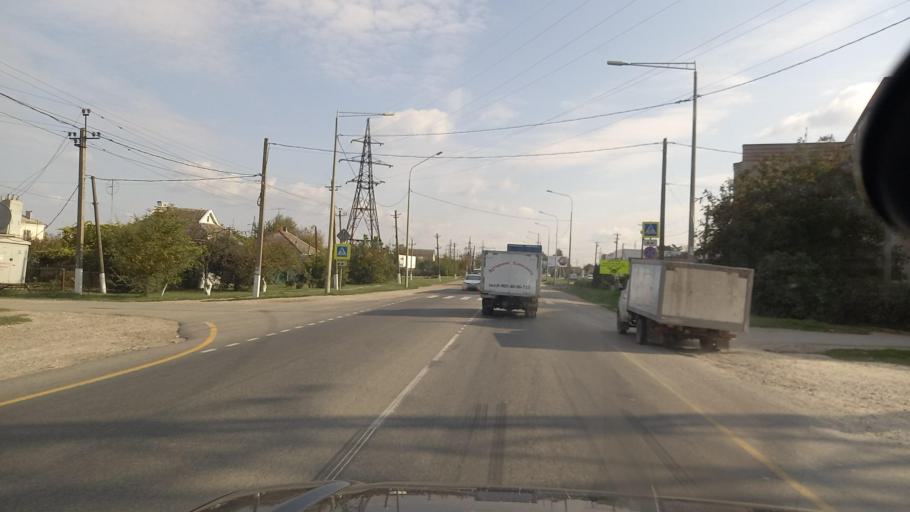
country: RU
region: Krasnodarskiy
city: Krymsk
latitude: 44.9061
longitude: 37.9891
